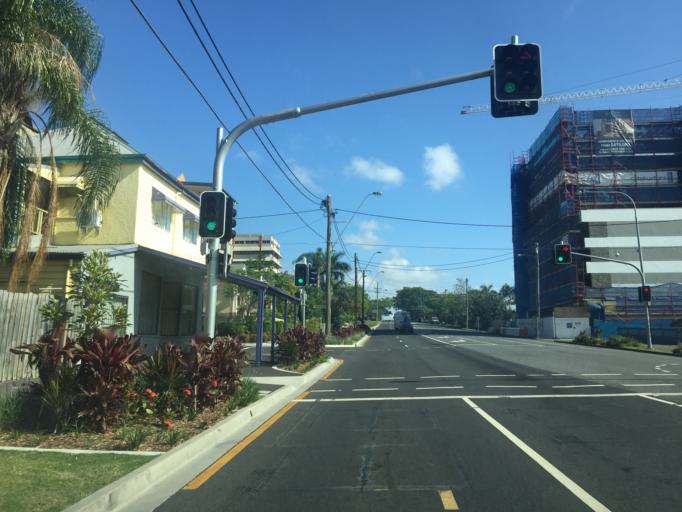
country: AU
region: Queensland
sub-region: Brisbane
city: Woolloongabba
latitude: -27.4796
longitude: 153.0357
